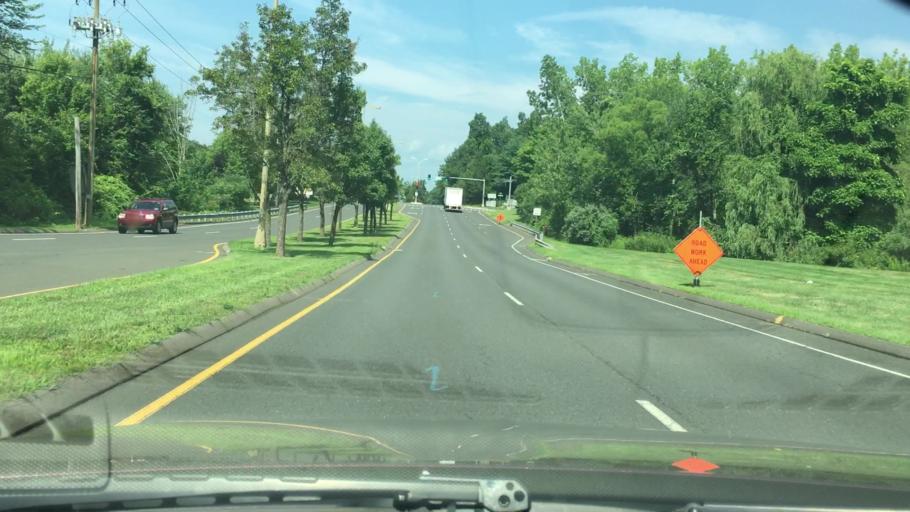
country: US
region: Connecticut
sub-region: Hartford County
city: Windsor
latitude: 41.8734
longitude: -72.6780
